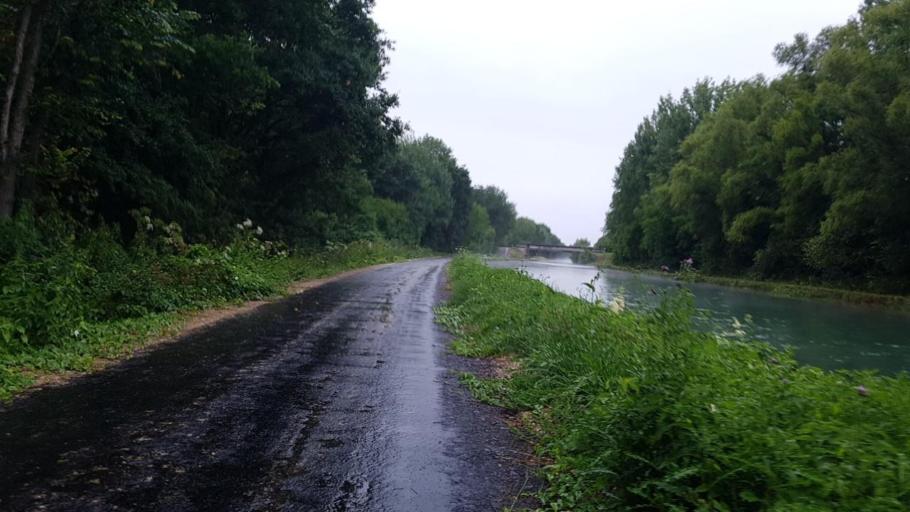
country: FR
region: Champagne-Ardenne
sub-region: Departement de la Marne
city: Sarry
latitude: 48.8697
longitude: 4.4574
